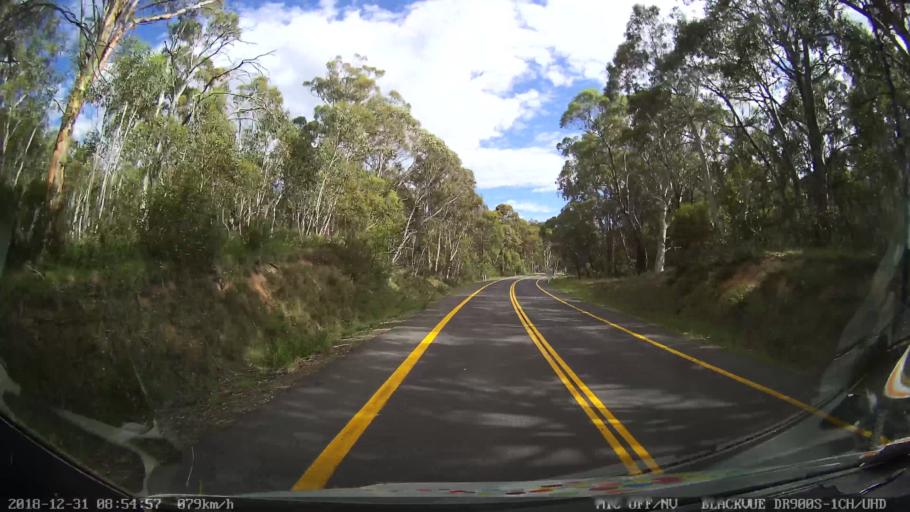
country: AU
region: New South Wales
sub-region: Snowy River
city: Jindabyne
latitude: -36.3490
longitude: 148.5633
